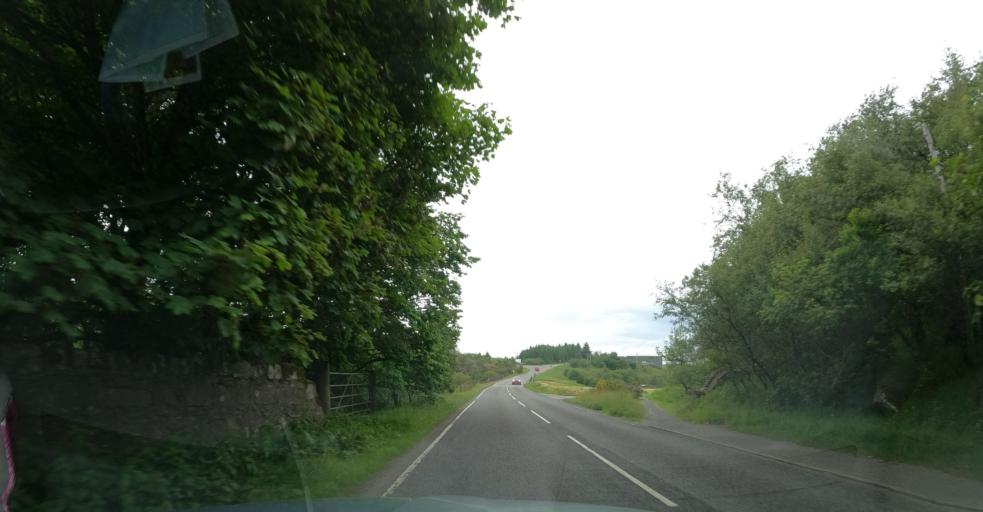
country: GB
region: Scotland
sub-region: Eilean Siar
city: Stornoway
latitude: 58.2054
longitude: -6.4197
